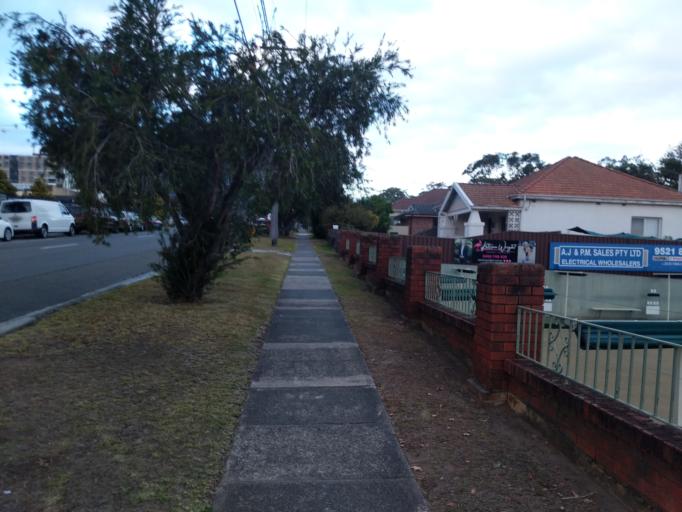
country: AU
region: New South Wales
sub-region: Sutherland Shire
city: Kirrawee
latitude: -34.0300
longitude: 151.0719
